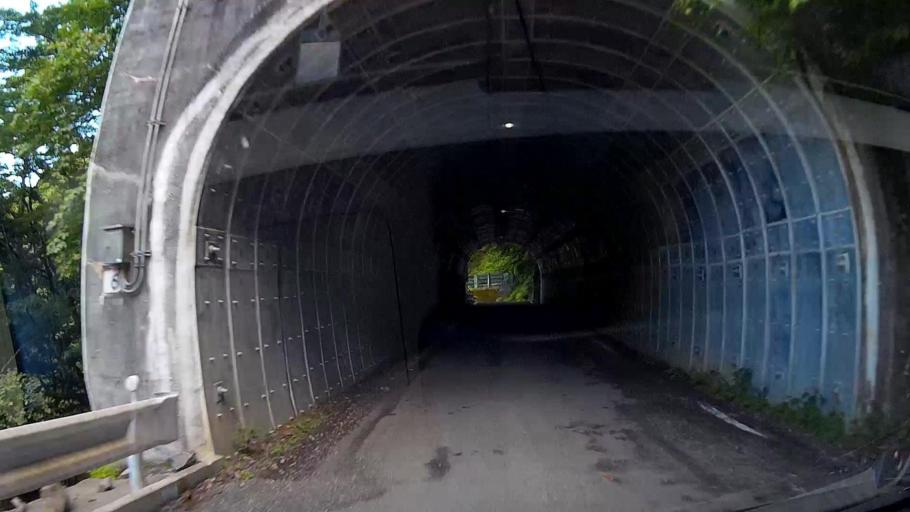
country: JP
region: Shizuoka
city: Shizuoka-shi
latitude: 35.2725
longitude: 138.2192
